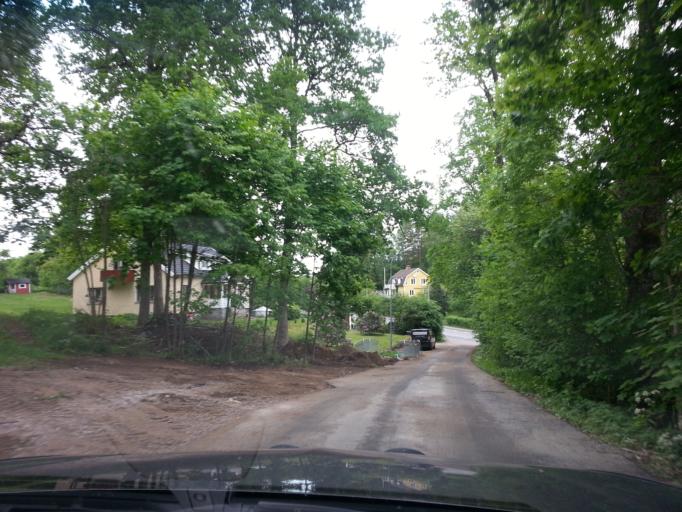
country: SE
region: Joenkoeping
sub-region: Vetlanda Kommun
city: Vetlanda
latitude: 57.2923
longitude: 15.1279
